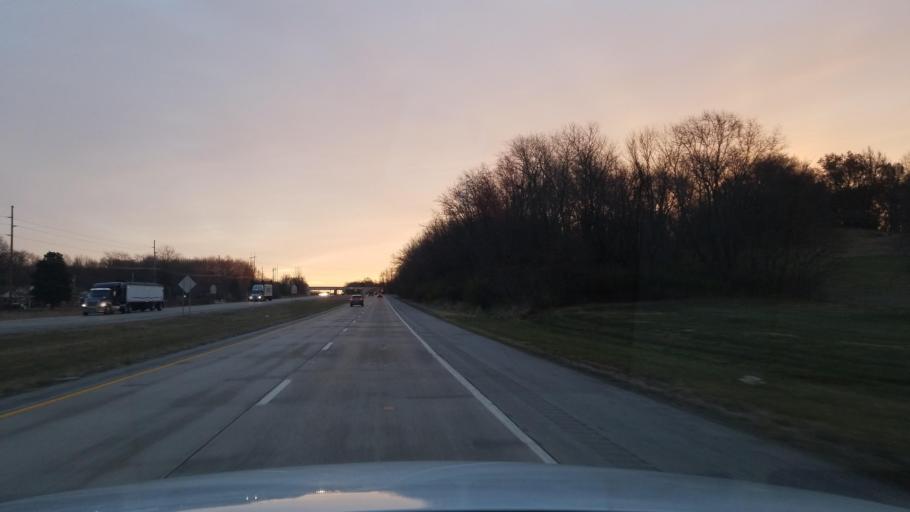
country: US
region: Indiana
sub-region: Posey County
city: Mount Vernon
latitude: 37.9417
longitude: -87.7455
